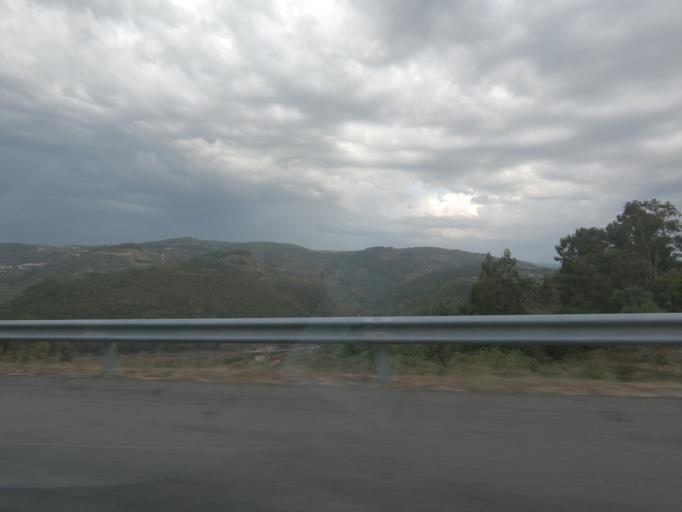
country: PT
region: Viseu
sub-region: Lamego
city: Lamego
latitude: 41.0915
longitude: -7.7833
